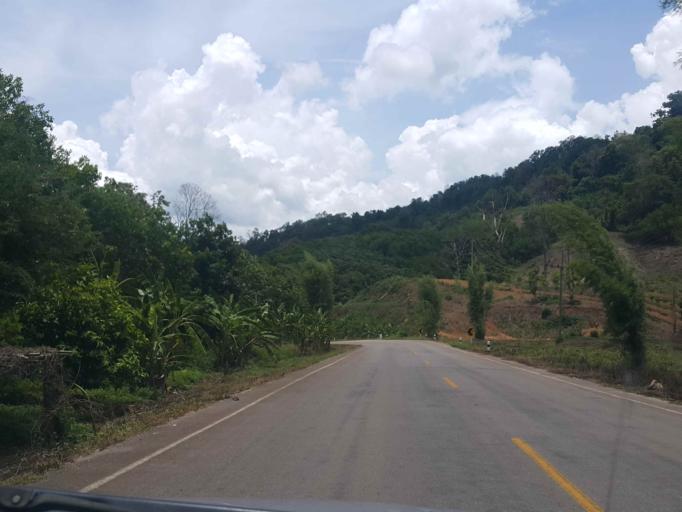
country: TH
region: Phayao
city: Chiang Muan
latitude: 18.9101
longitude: 100.1171
